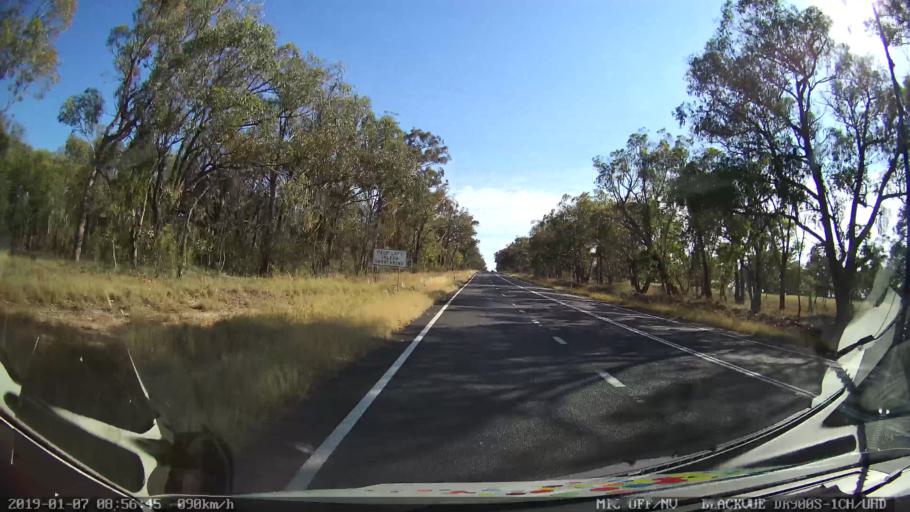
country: AU
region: New South Wales
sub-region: Tamworth Municipality
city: Kootingal
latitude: -30.7755
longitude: 151.3467
